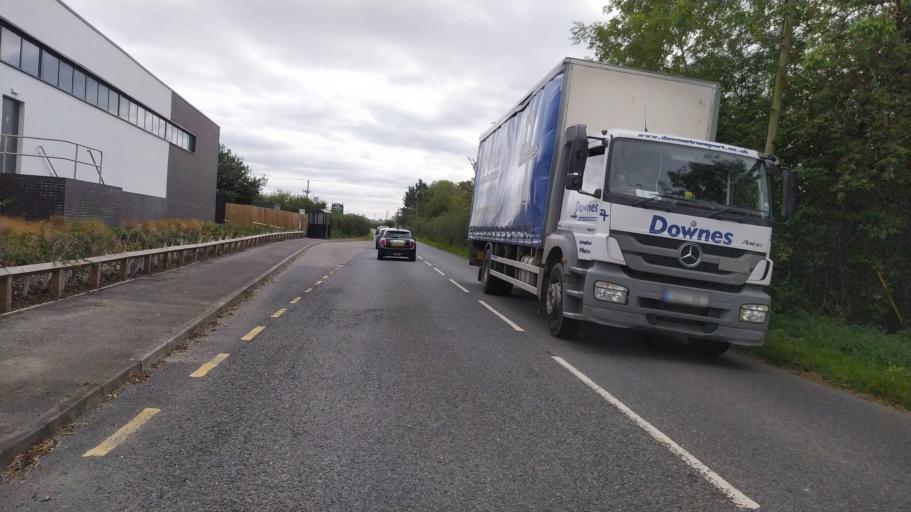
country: GB
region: England
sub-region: Dorset
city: Gillingham
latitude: 51.0286
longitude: -2.2571
